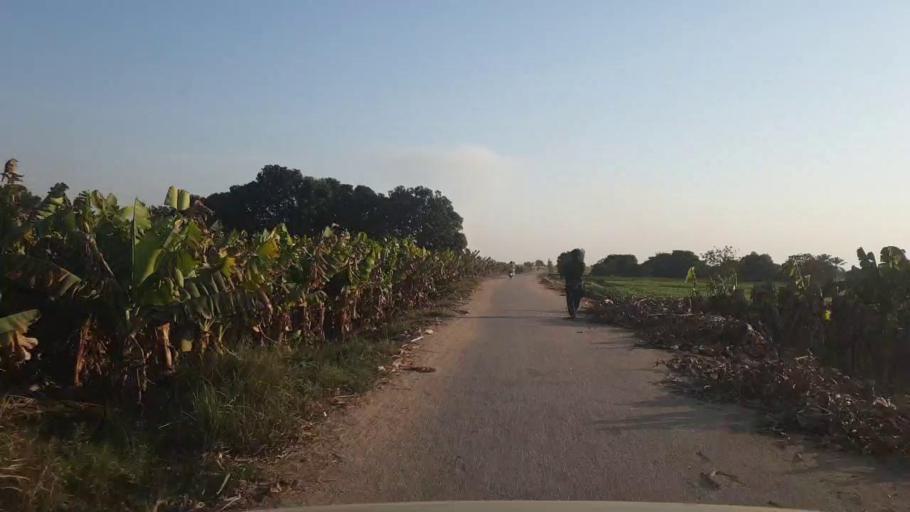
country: PK
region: Sindh
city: Chambar
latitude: 25.2859
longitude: 68.8974
